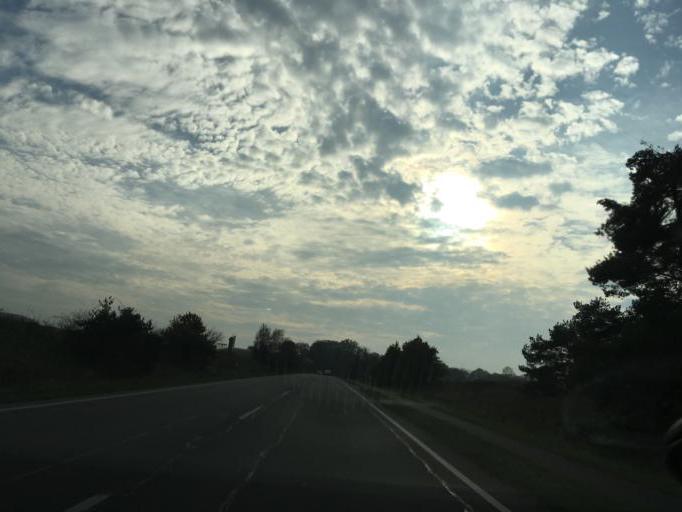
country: DE
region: Lower Saxony
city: Betzendorf
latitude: 53.1563
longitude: 10.2991
